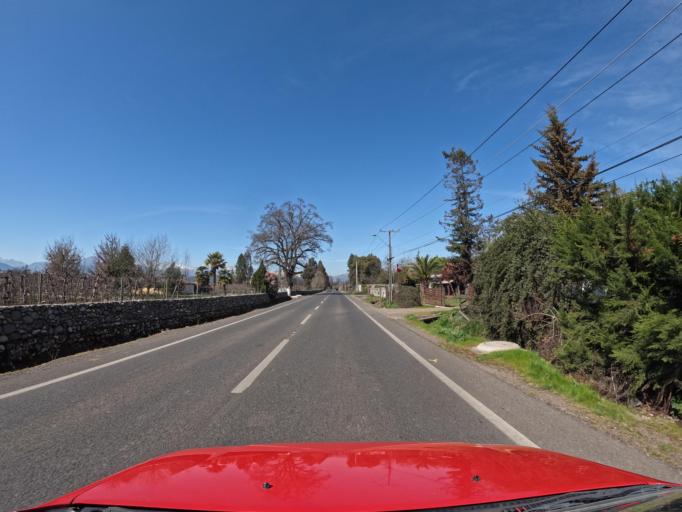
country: CL
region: Maule
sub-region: Provincia de Curico
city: Teno
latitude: -34.9682
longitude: -71.0275
